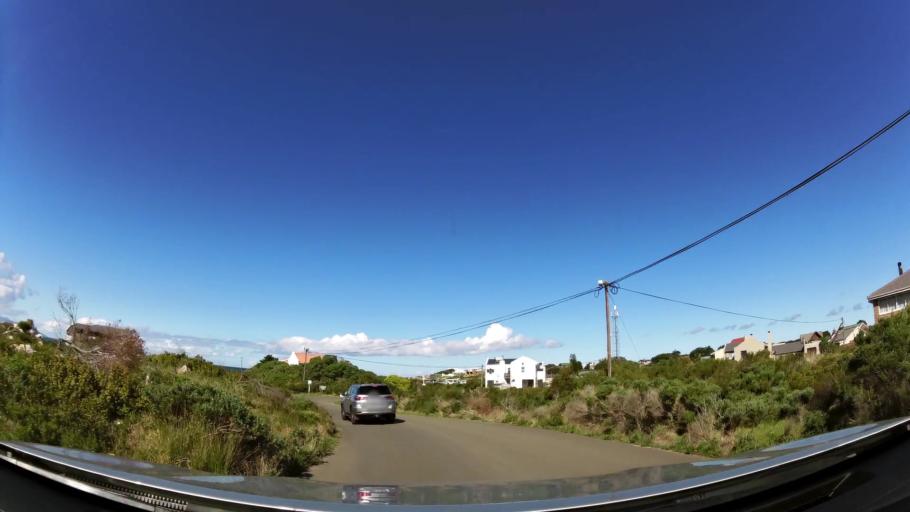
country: ZA
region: Western Cape
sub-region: Overberg District Municipality
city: Grabouw
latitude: -34.3700
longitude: 18.8918
